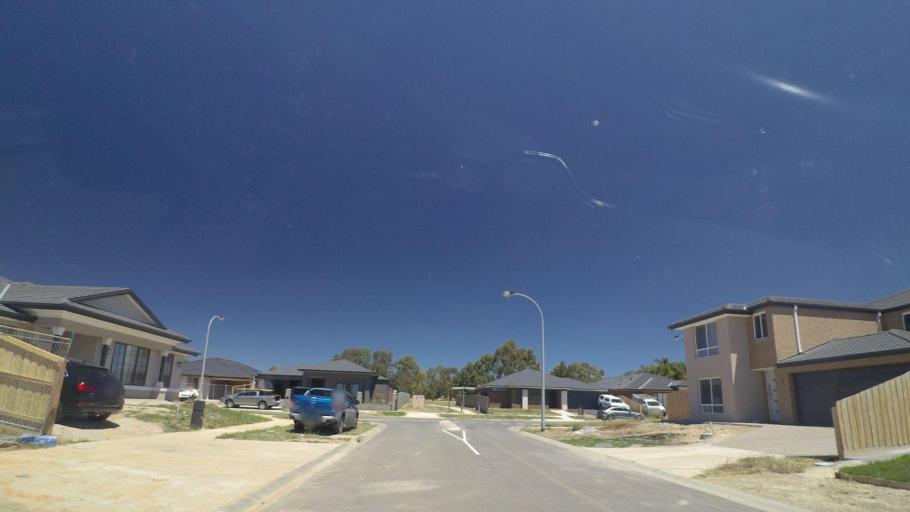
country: AU
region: Victoria
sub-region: Yarra Ranges
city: Lilydale
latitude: -37.7398
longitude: 145.3477
